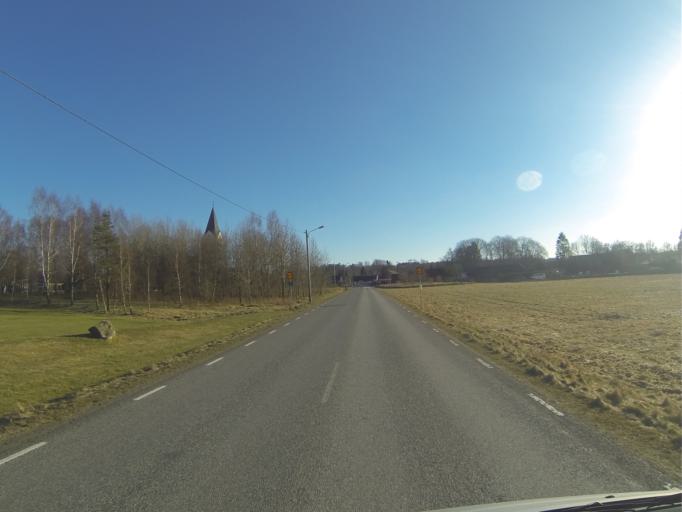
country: SE
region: Skane
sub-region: Horby Kommun
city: Hoerby
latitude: 55.9261
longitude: 13.6682
